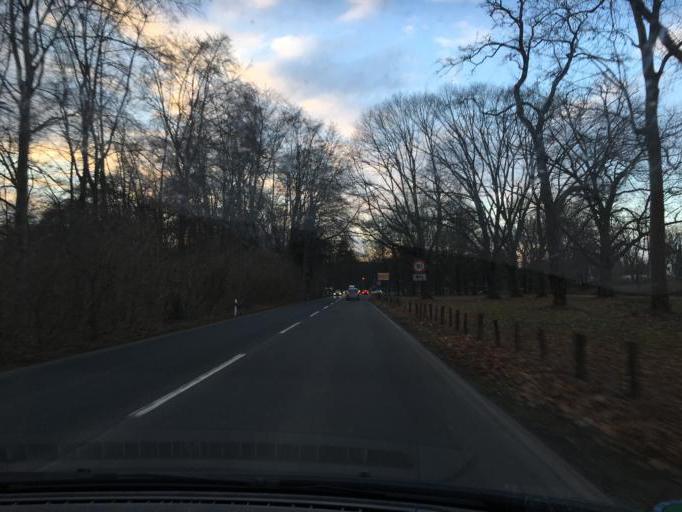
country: DE
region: North Rhine-Westphalia
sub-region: Regierungsbezirk Koln
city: Neustadt/Sued
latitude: 50.9133
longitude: 6.8990
